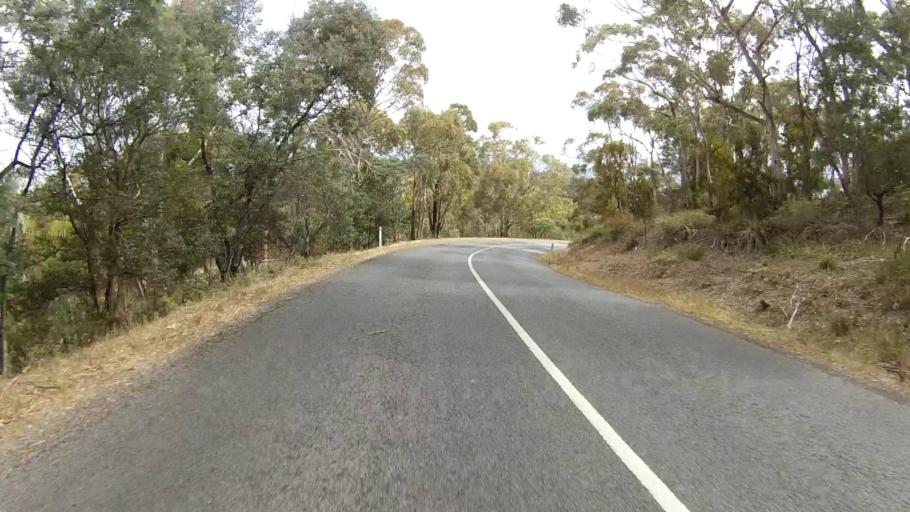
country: AU
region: Tasmania
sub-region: Clarence
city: Howrah
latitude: -42.8581
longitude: 147.4187
